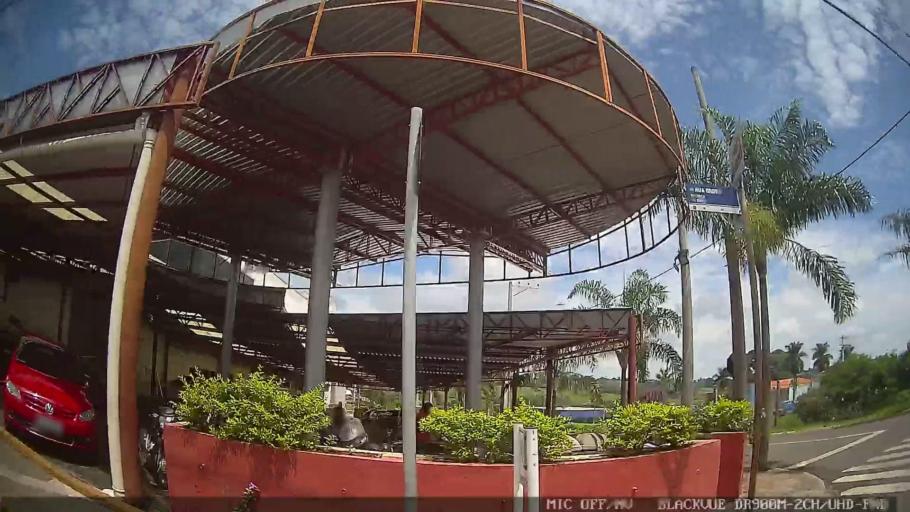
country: BR
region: Sao Paulo
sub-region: Laranjal Paulista
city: Laranjal Paulista
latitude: -23.0445
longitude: -47.8364
